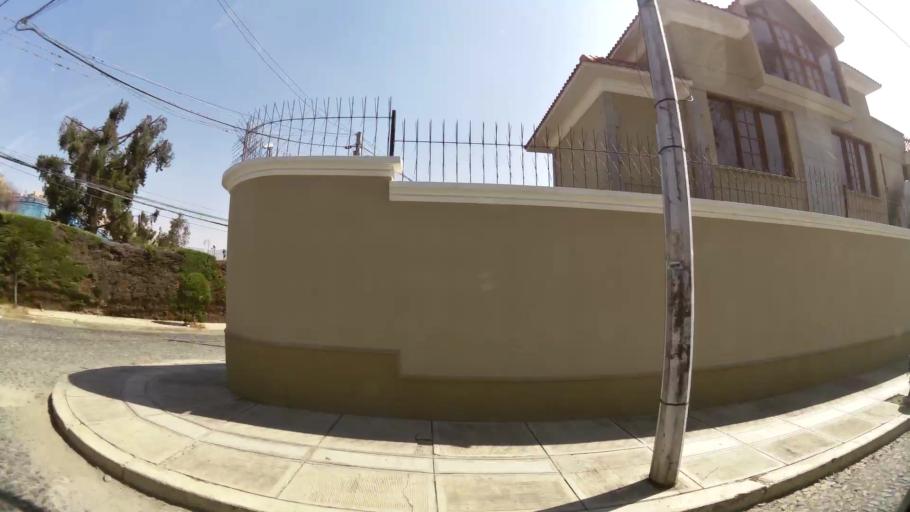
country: BO
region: La Paz
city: La Paz
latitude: -16.5431
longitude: -68.0818
